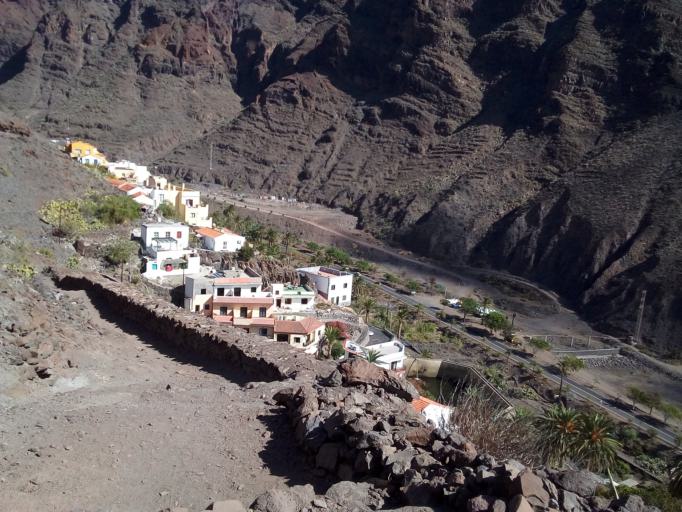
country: ES
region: Canary Islands
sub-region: Provincia de Santa Cruz de Tenerife
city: Alajero
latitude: 28.0978
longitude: -17.3345
